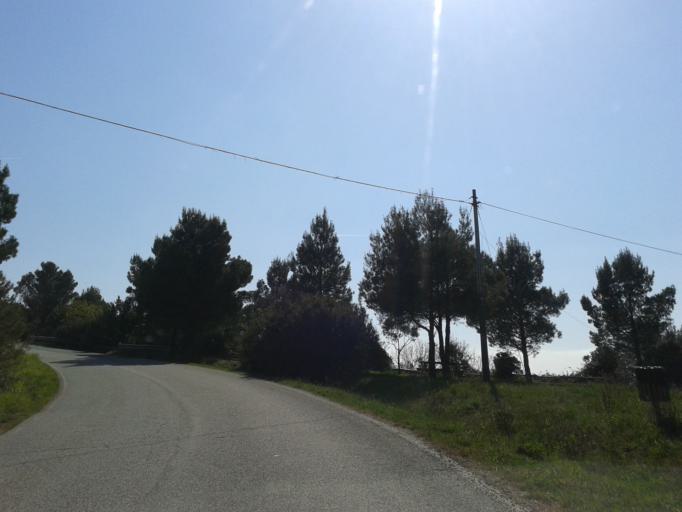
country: IT
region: Tuscany
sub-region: Provincia di Livorno
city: Quercianella
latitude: 43.4502
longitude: 10.3896
